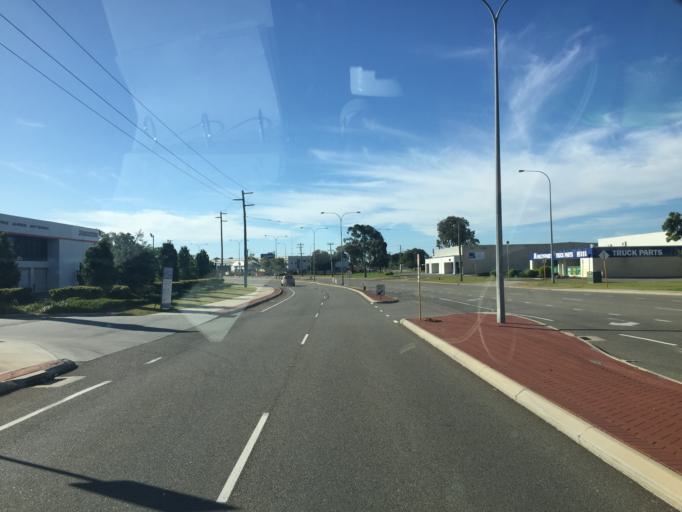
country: AU
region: Western Australia
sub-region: Belmont
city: Kewdale
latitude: -31.9794
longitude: 115.9592
